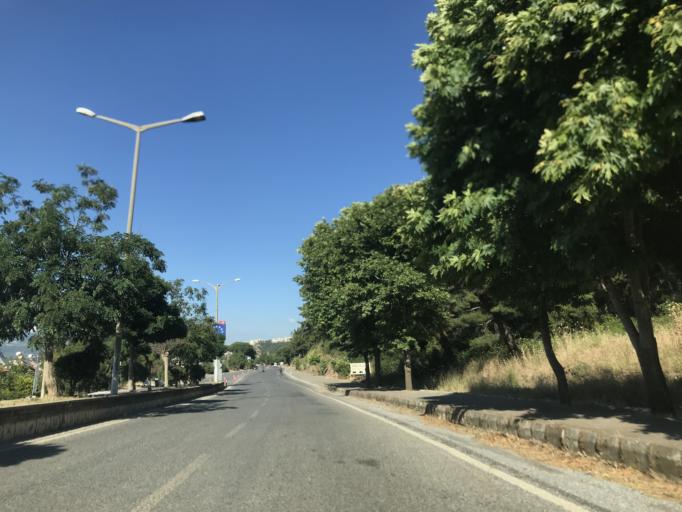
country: TR
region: Aydin
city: Davutlar
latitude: 37.7159
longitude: 27.2344
